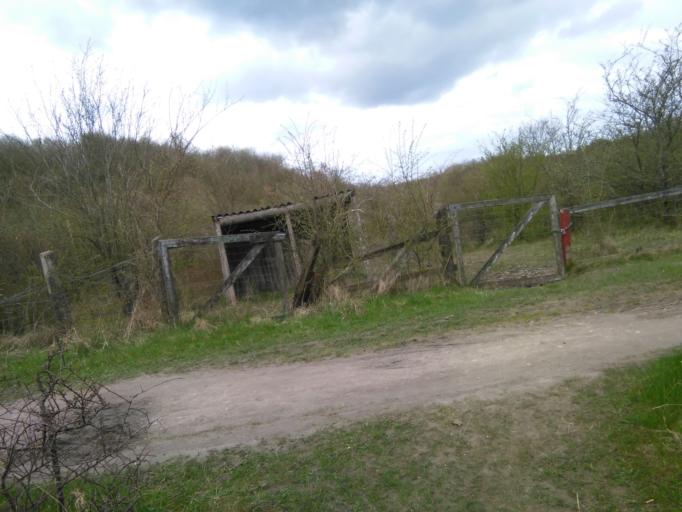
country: DK
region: Central Jutland
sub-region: Arhus Kommune
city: Stavtrup
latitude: 56.1672
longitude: 10.1322
